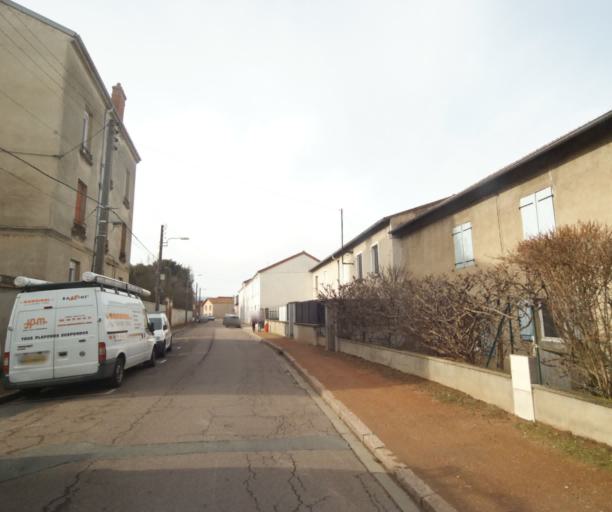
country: FR
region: Rhone-Alpes
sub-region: Departement de la Loire
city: Roanne
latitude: 46.0304
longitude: 4.0564
